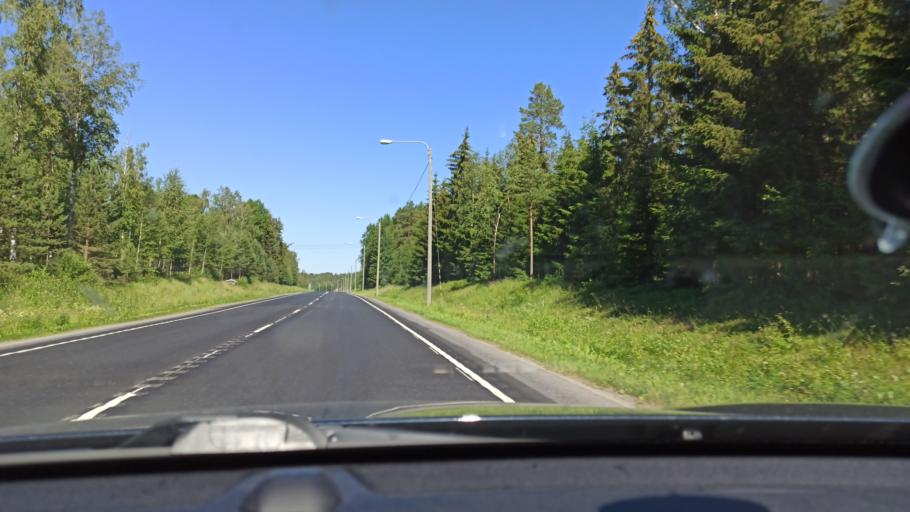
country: FI
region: Ostrobothnia
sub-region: Vaasa
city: Oravais
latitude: 63.2816
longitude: 22.3540
